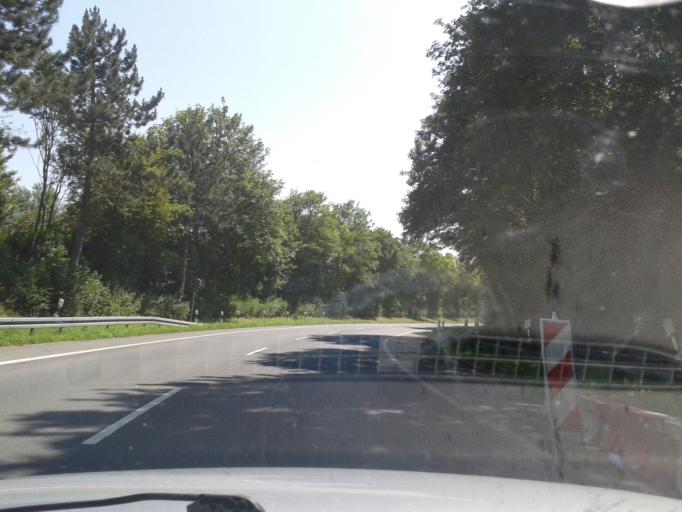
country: DE
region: North Rhine-Westphalia
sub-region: Regierungsbezirk Detmold
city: Paderborn
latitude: 51.7306
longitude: 8.7754
